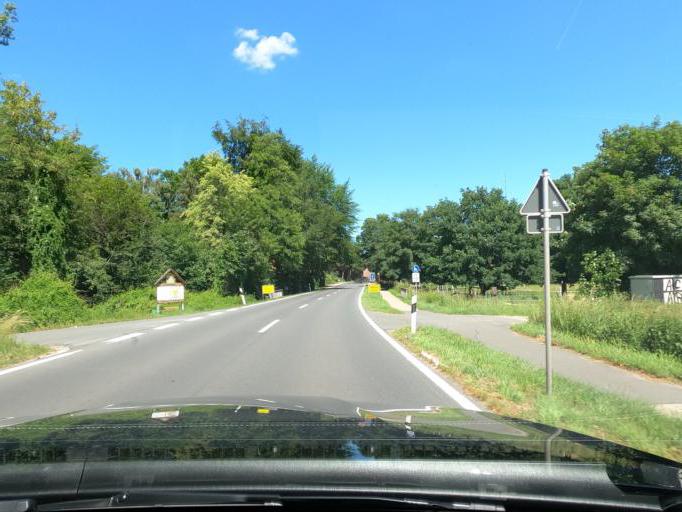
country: DE
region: Lower Saxony
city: Lehrte
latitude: 52.4143
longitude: 9.9771
